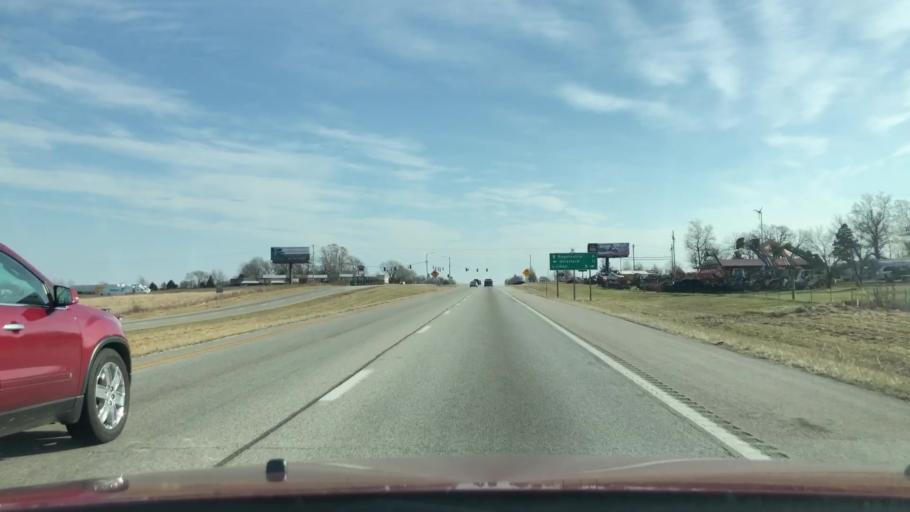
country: US
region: Missouri
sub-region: Webster County
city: Rogersville
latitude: 37.1187
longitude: -93.1228
